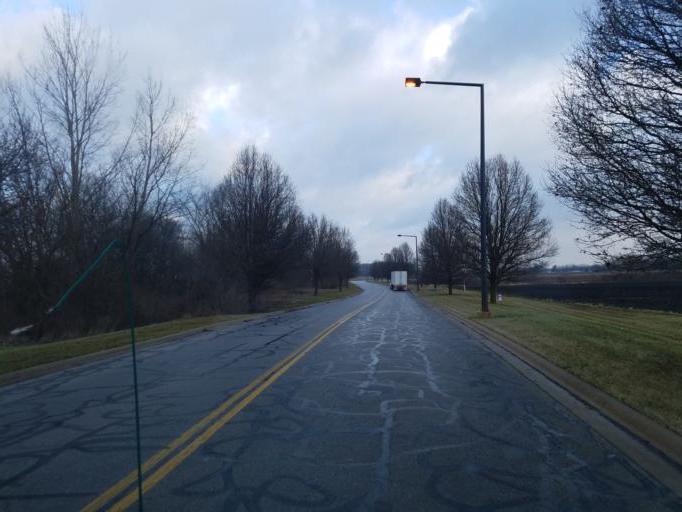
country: US
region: Ohio
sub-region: Marion County
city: Marion
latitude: 40.6120
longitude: -83.1408
